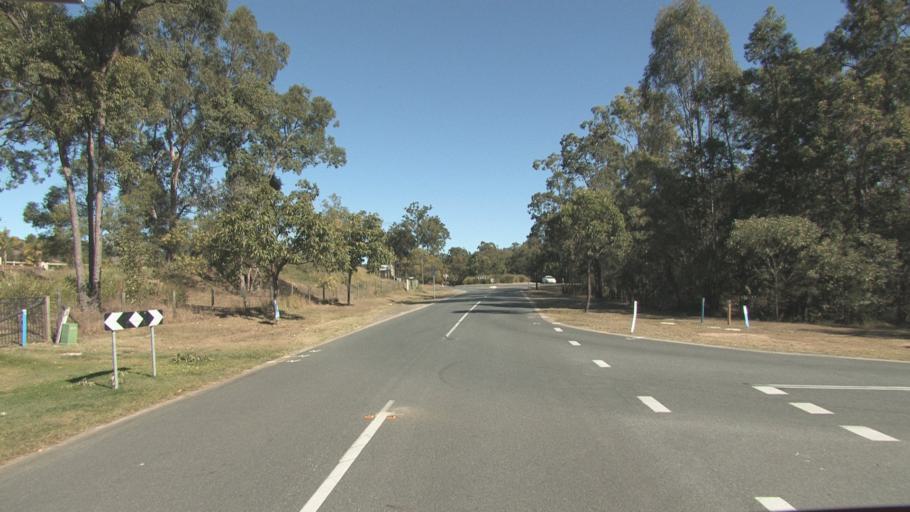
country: AU
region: Queensland
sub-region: Logan
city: North Maclean
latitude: -27.7524
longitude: 152.9572
